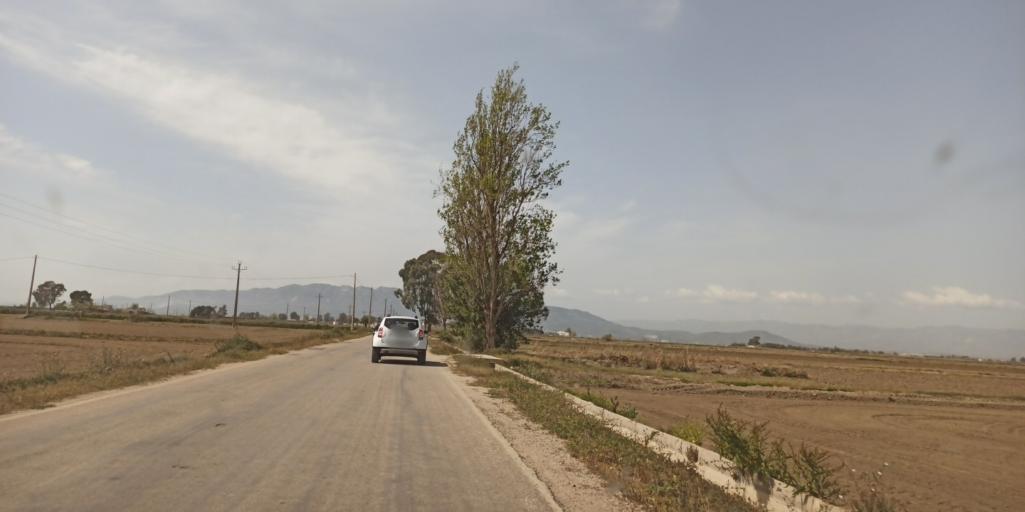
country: ES
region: Catalonia
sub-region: Provincia de Tarragona
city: Deltebre
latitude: 40.6465
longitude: 0.7012
